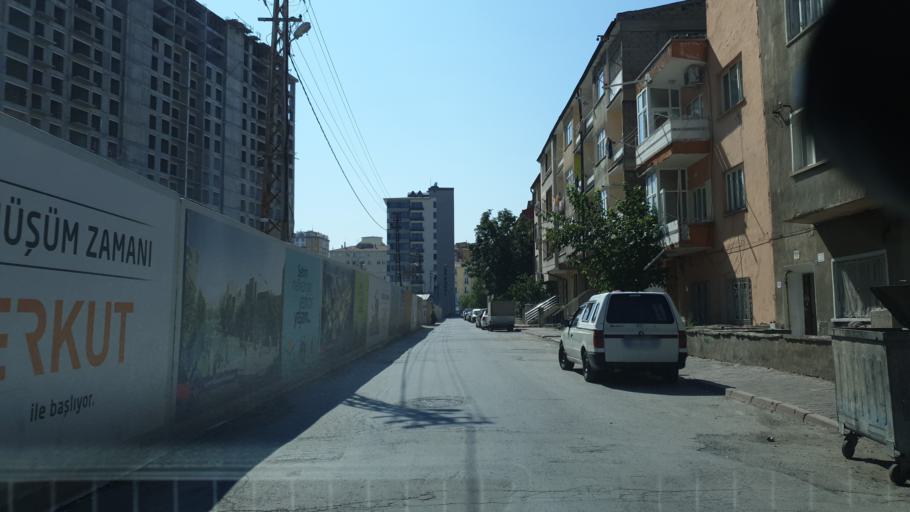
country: TR
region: Kayseri
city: Kayseri
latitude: 38.7282
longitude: 35.4896
